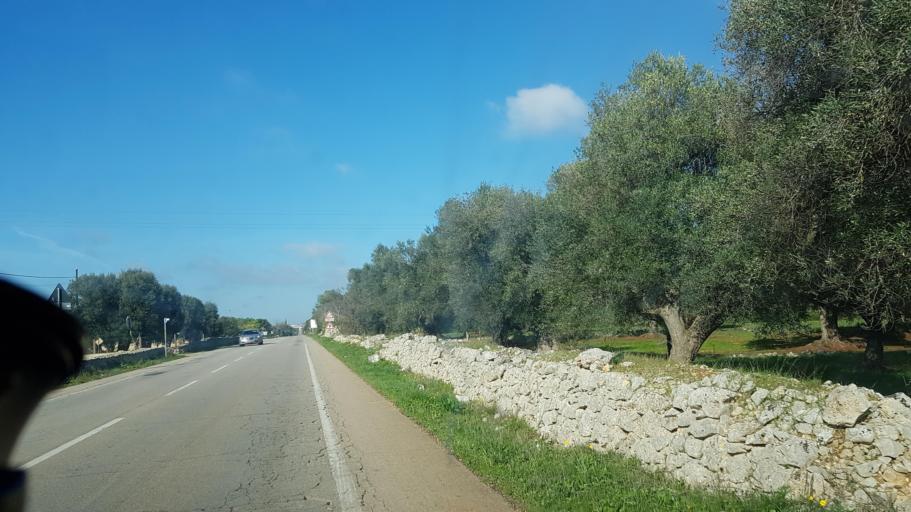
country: IT
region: Apulia
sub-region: Provincia di Brindisi
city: San Vito dei Normanni
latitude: 40.6751
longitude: 17.6894
